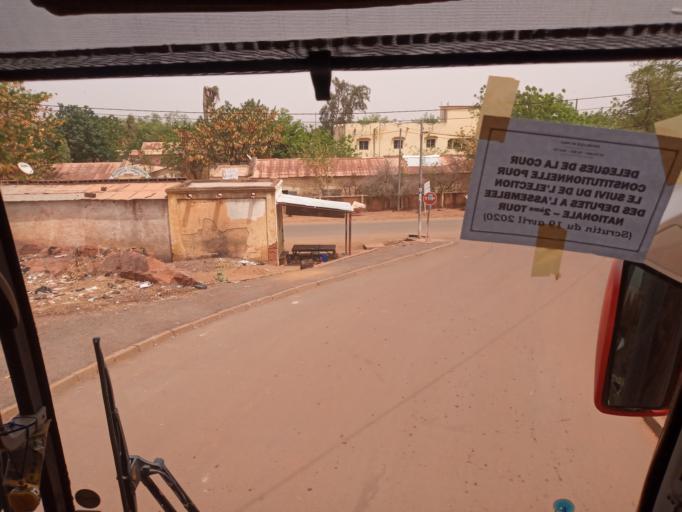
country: ML
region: Koulikoro
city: Koulikoro
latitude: 12.8595
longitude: -7.5601
